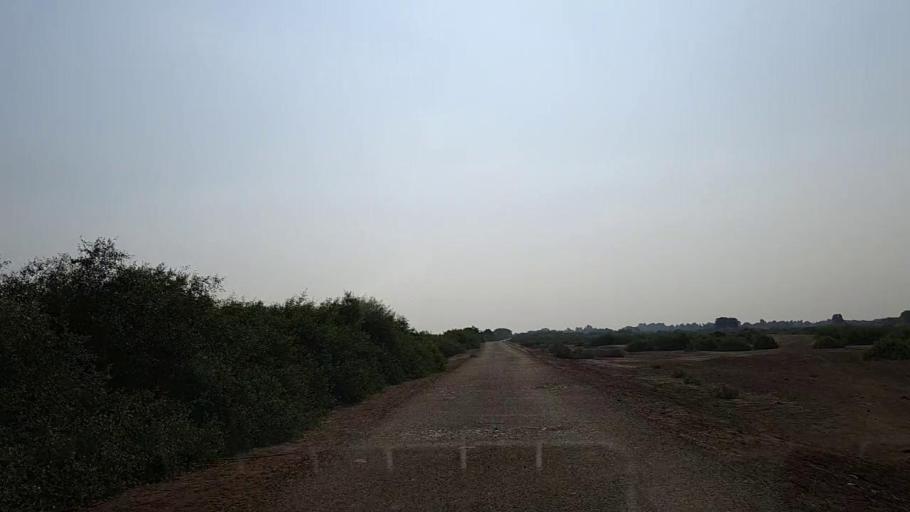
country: PK
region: Sindh
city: Mirpur Sakro
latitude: 24.6365
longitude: 67.6610
